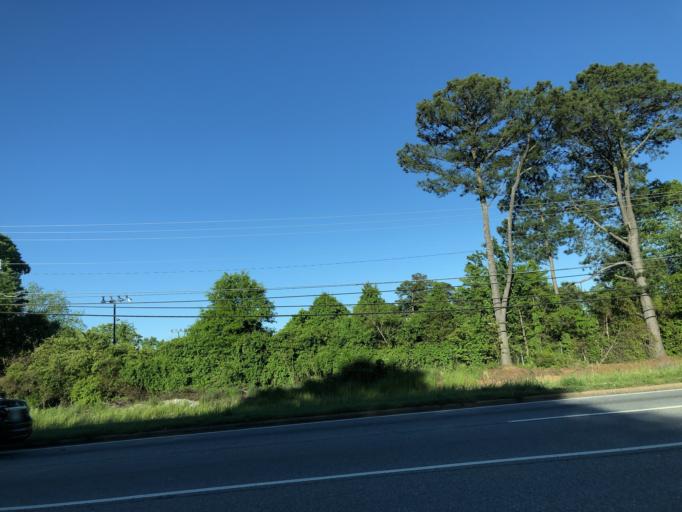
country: US
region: Georgia
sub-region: Clarke County
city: Country Club Estates
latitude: 33.9762
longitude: -83.4143
